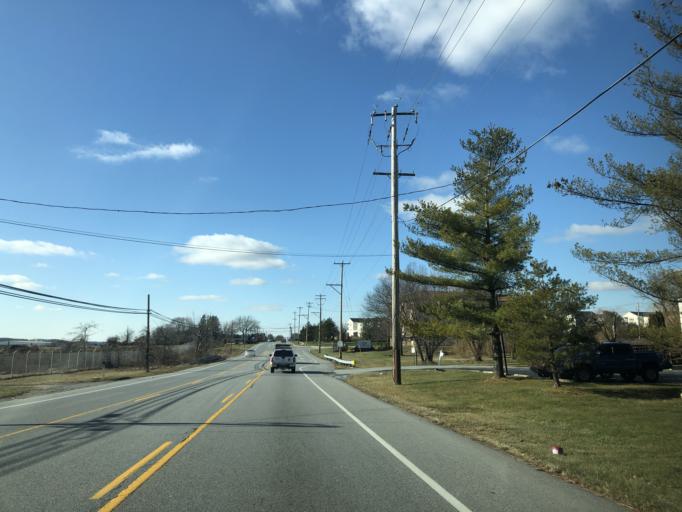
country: US
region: Pennsylvania
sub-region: Chester County
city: Coatesville
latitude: 39.9833
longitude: -75.8721
